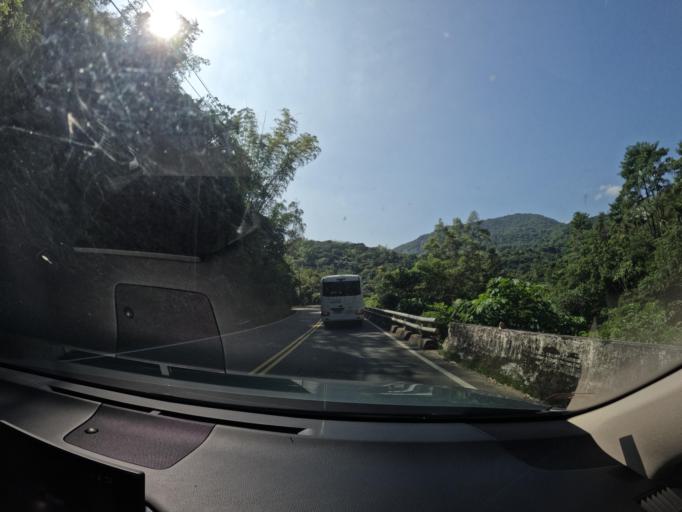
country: TW
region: Taiwan
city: Yujing
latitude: 23.0710
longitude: 120.6504
